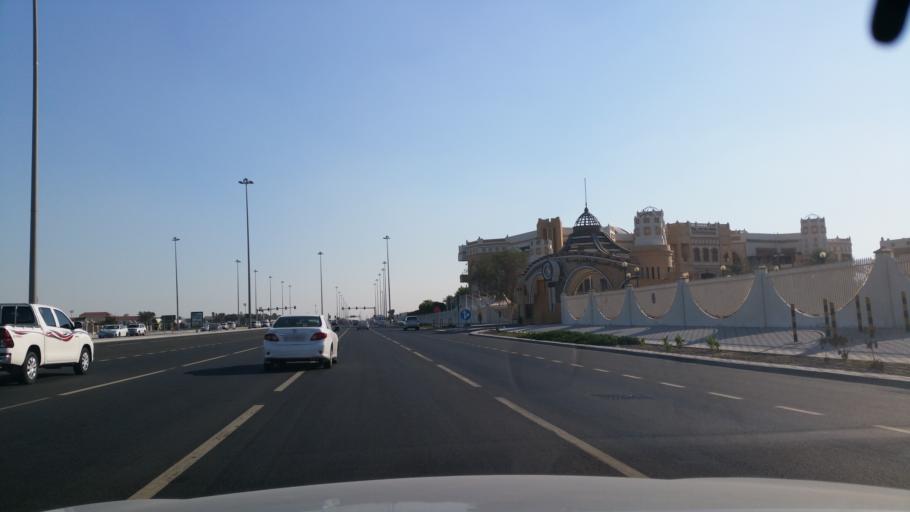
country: QA
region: Baladiyat ar Rayyan
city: Ar Rayyan
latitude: 25.2727
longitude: 51.4311
